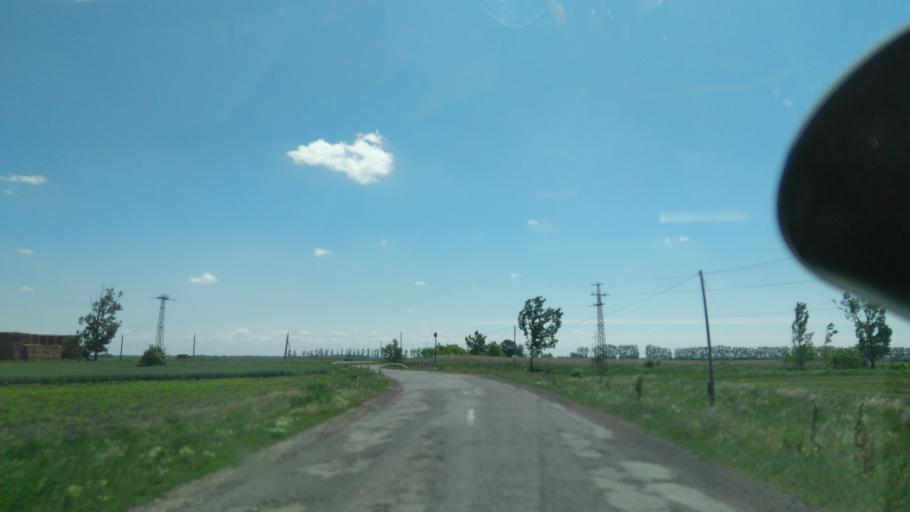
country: HU
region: Bekes
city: Kunagota
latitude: 46.4089
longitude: 21.0554
